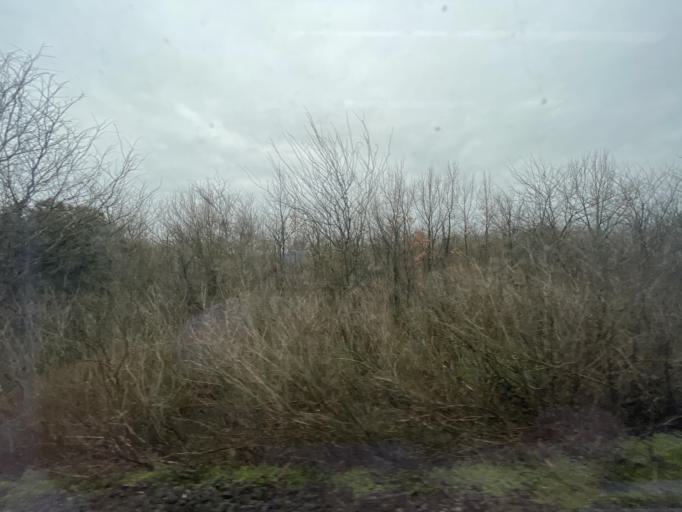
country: GE
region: Imereti
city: K'ulashi
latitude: 42.1858
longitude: 42.4533
